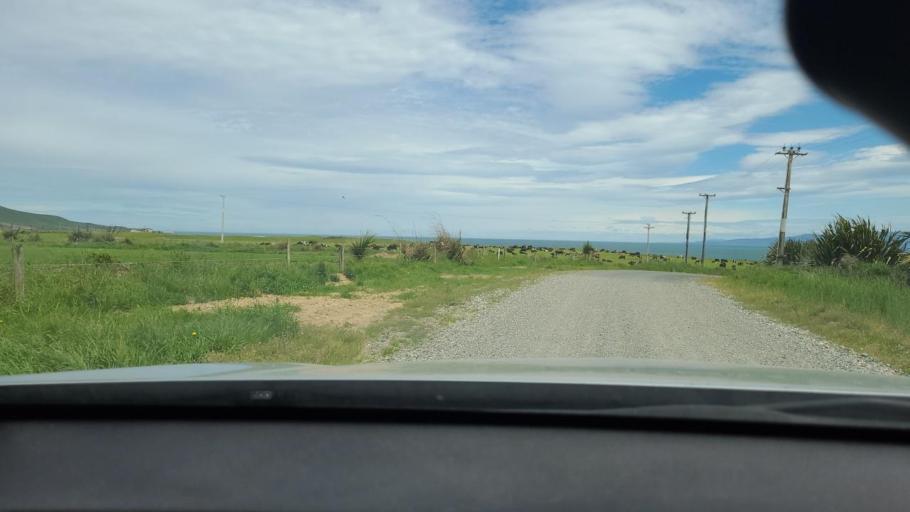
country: NZ
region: Southland
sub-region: Southland District
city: Riverton
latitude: -46.2870
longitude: 167.7406
